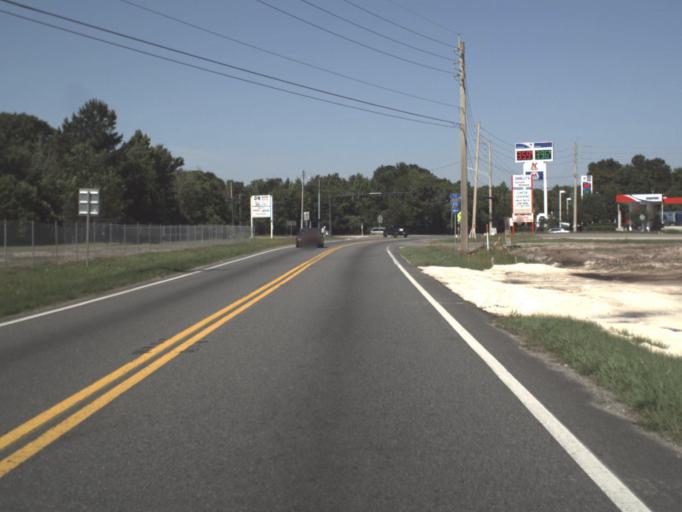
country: US
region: Florida
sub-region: Duval County
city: Baldwin
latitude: 30.3148
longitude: -81.8470
